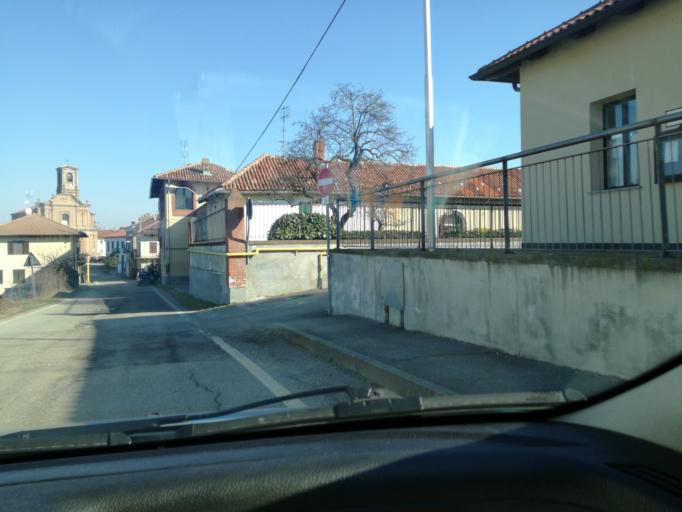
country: IT
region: Piedmont
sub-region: Provincia di Torino
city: Verrua Savoia
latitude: 45.1595
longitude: 8.0950
